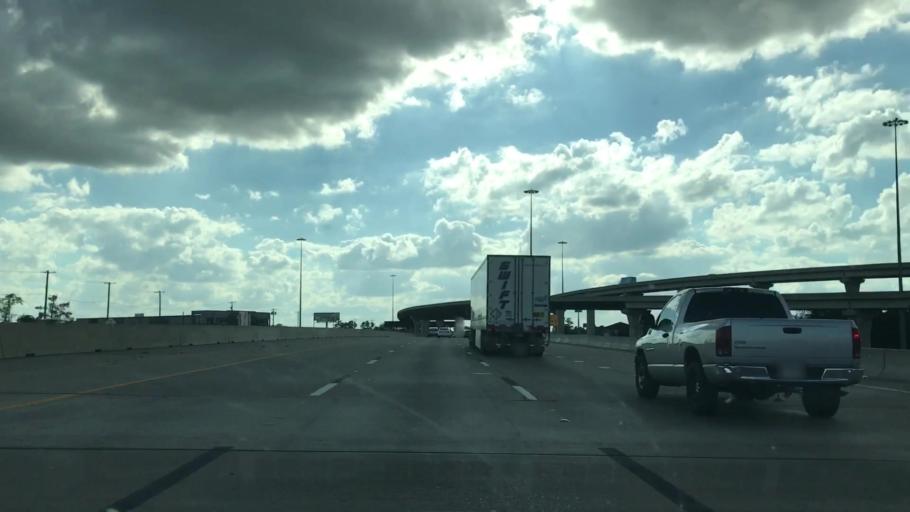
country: US
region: Texas
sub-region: Dallas County
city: Rowlett
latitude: 32.8569
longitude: -96.5548
